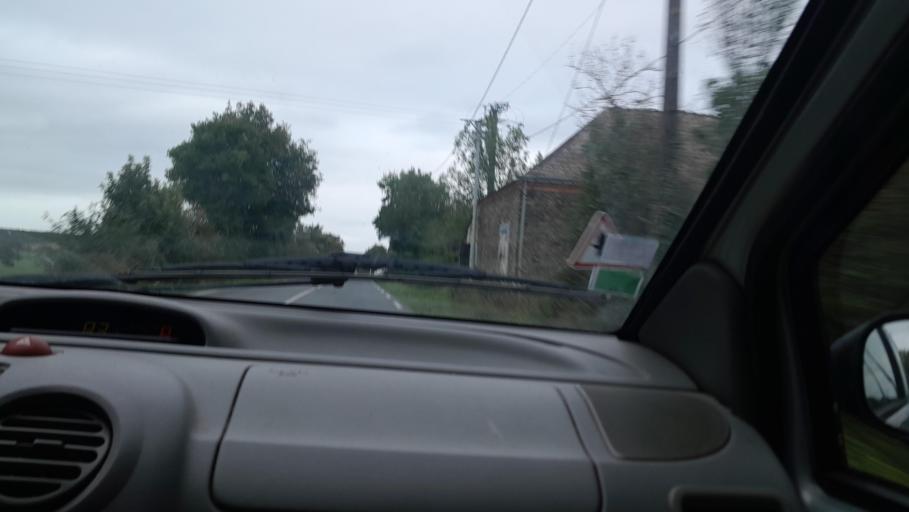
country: FR
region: Pays de la Loire
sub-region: Departement de Maine-et-Loire
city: Pouance
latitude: 47.6542
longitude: -1.1990
